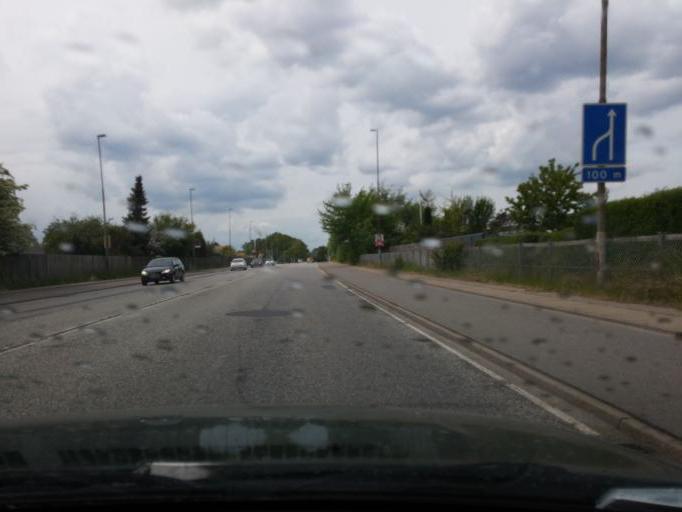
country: DK
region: South Denmark
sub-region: Odense Kommune
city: Odense
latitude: 55.4107
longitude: 10.3311
